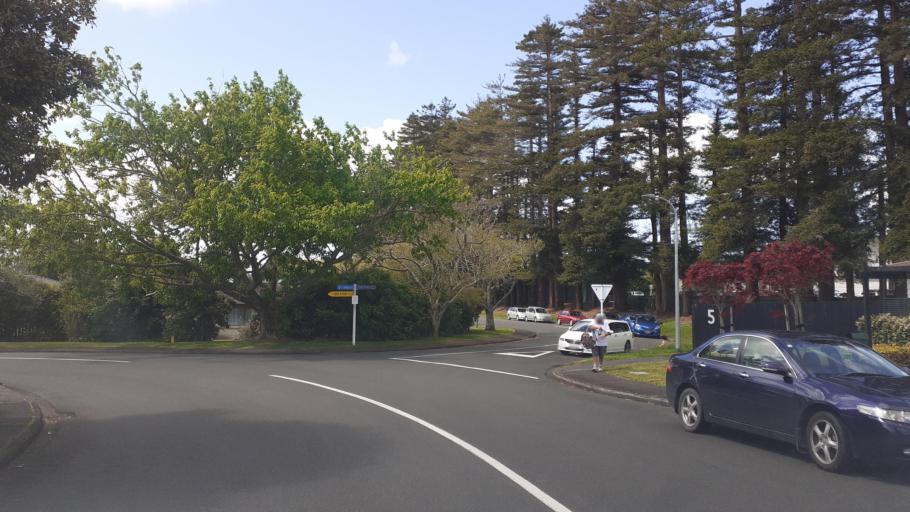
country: NZ
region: Northland
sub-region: Far North District
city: Kerikeri
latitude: -35.2257
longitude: 173.9516
